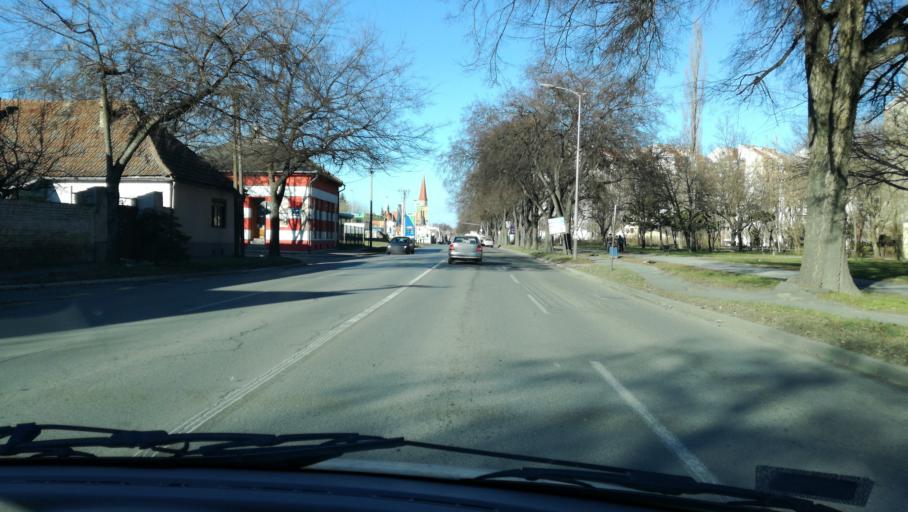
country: RS
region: Autonomna Pokrajina Vojvodina
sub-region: Severnobacki Okrug
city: Subotica
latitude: 46.0849
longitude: 19.6714
